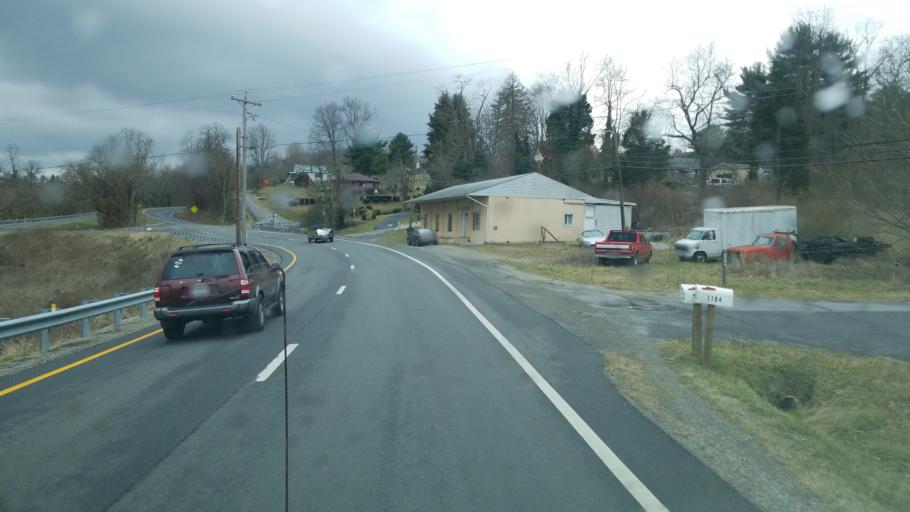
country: US
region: Virginia
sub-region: Giles County
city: Pearisburg
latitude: 37.3059
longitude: -80.7373
